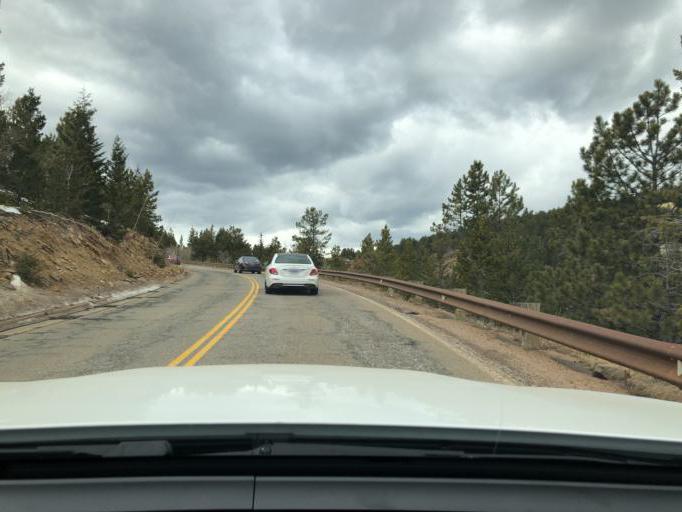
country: US
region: Colorado
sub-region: Gilpin County
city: Central City
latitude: 39.7935
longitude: -105.5126
